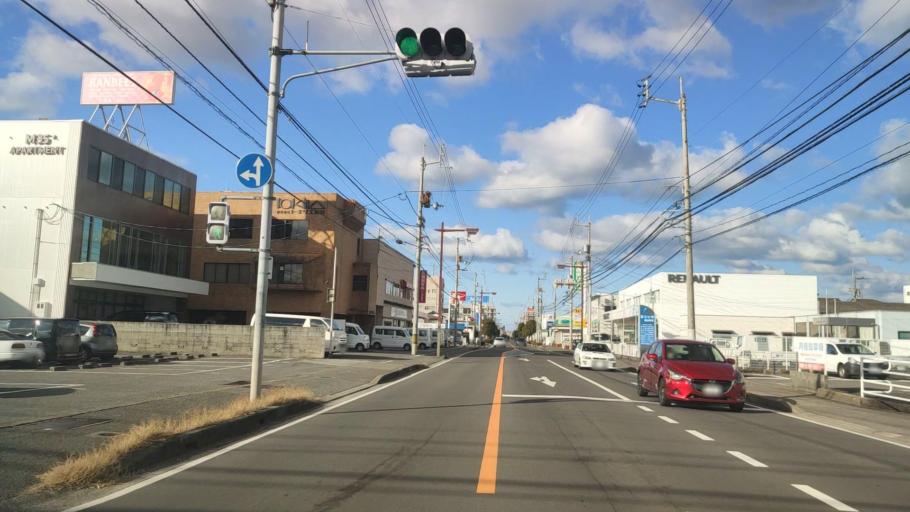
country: JP
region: Ehime
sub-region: Shikoku-chuo Shi
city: Matsuyama
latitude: 33.8285
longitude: 132.7430
